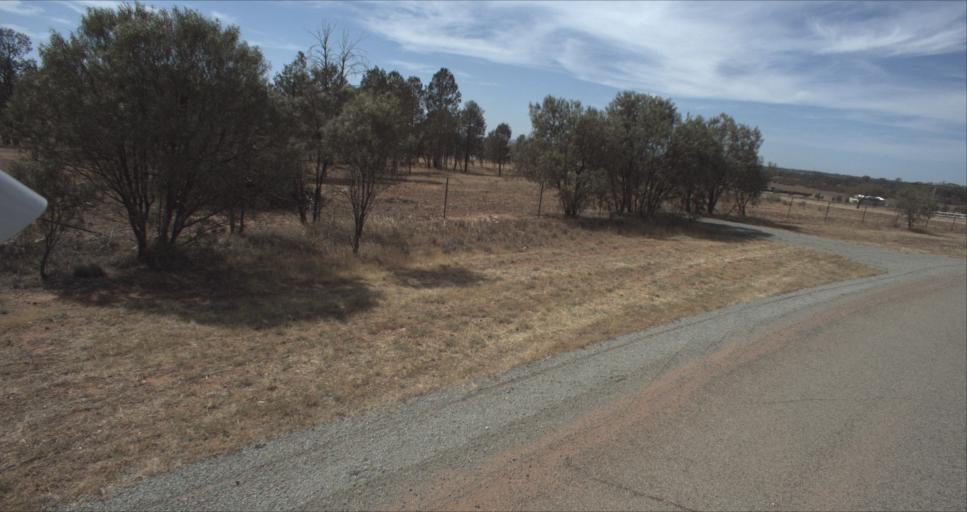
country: AU
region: New South Wales
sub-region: Leeton
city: Leeton
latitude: -34.5753
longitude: 146.4514
